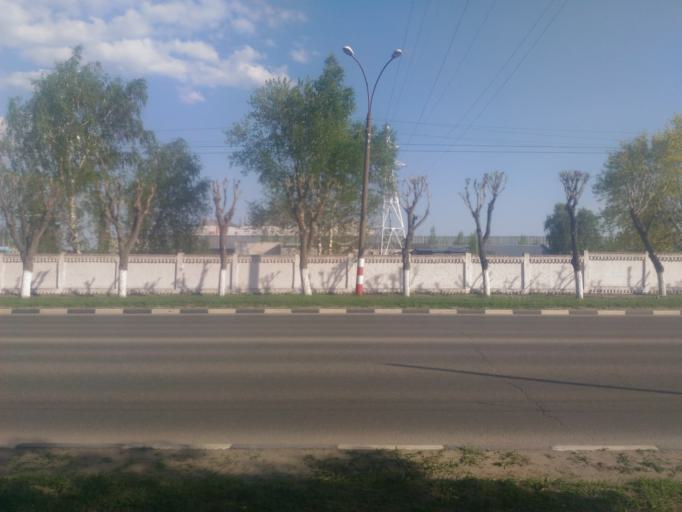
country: RU
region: Ulyanovsk
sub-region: Ulyanovskiy Rayon
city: Ulyanovsk
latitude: 54.2839
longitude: 48.3540
